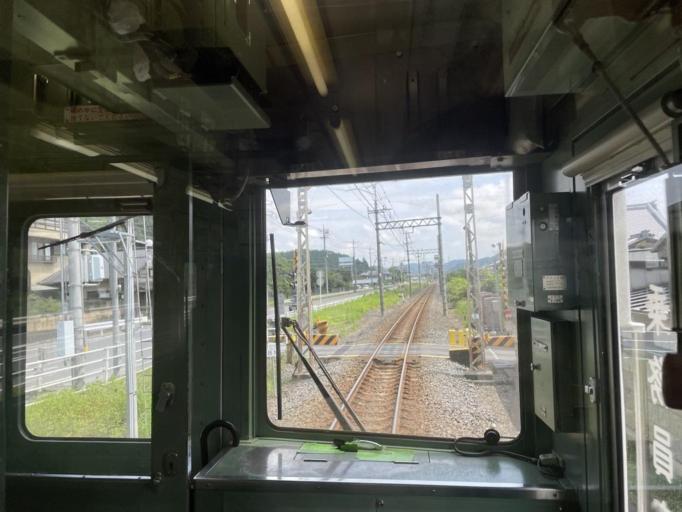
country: JP
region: Tochigi
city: Tanuma
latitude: 36.3814
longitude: 139.5951
